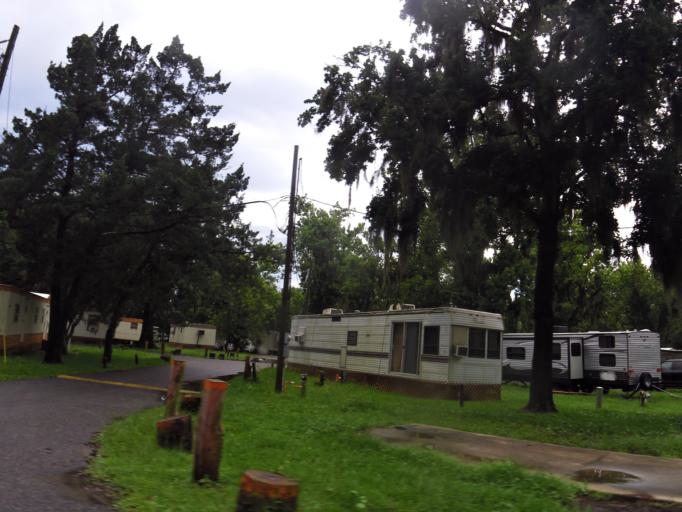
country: US
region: Florida
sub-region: Duval County
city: Jacksonville
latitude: 30.2771
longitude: -81.6246
